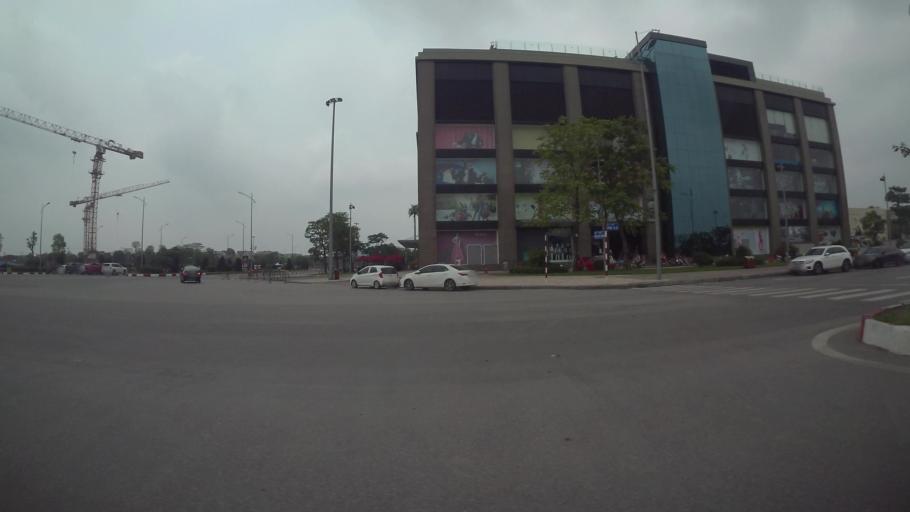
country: VN
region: Ha Noi
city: Trau Quy
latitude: 21.0512
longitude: 105.9173
